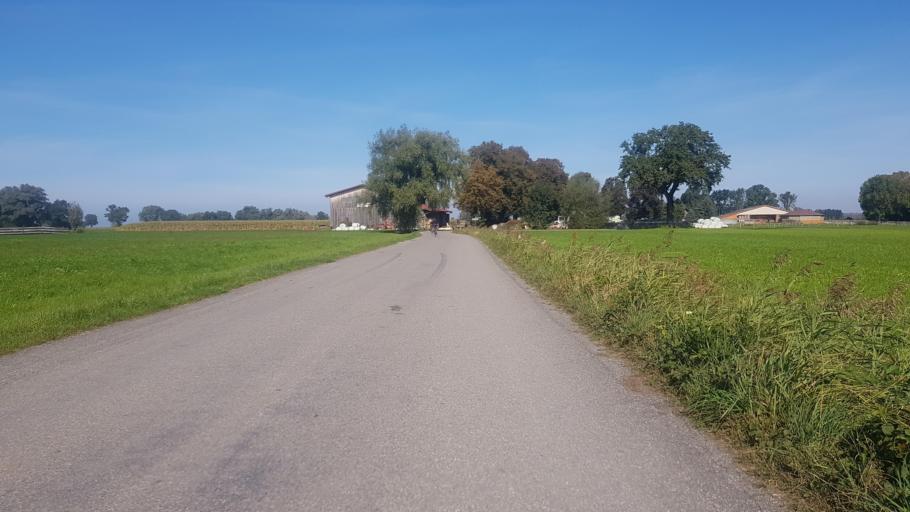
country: AT
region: Vorarlberg
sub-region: Politischer Bezirk Bregenz
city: Gaissau
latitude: 47.4766
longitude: 9.6214
